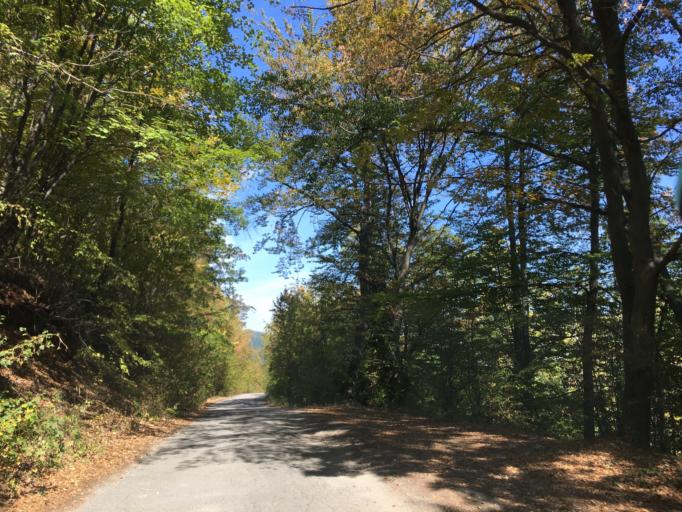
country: BG
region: Pazardzhik
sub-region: Obshtina Peshtera
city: Peshtera
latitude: 42.0080
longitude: 24.2779
